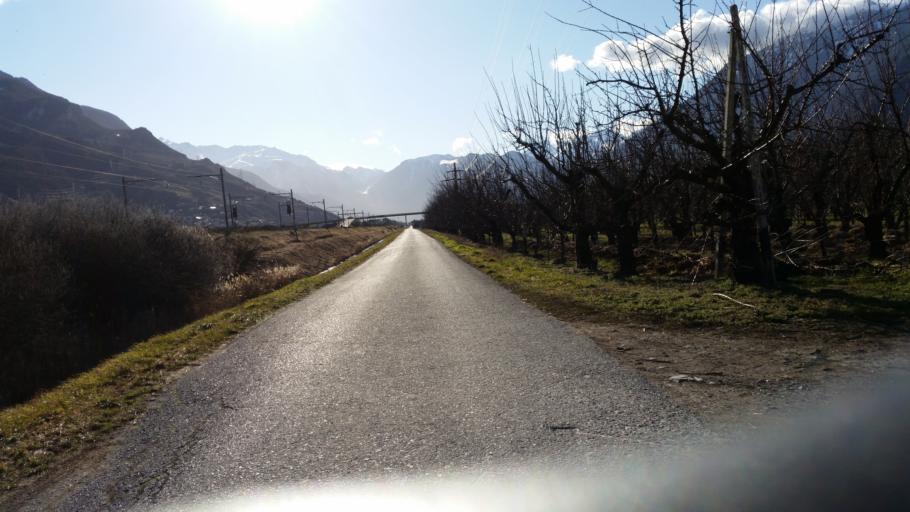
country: CH
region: Valais
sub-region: Martigny District
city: Saillon
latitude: 46.1616
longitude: 7.1981
